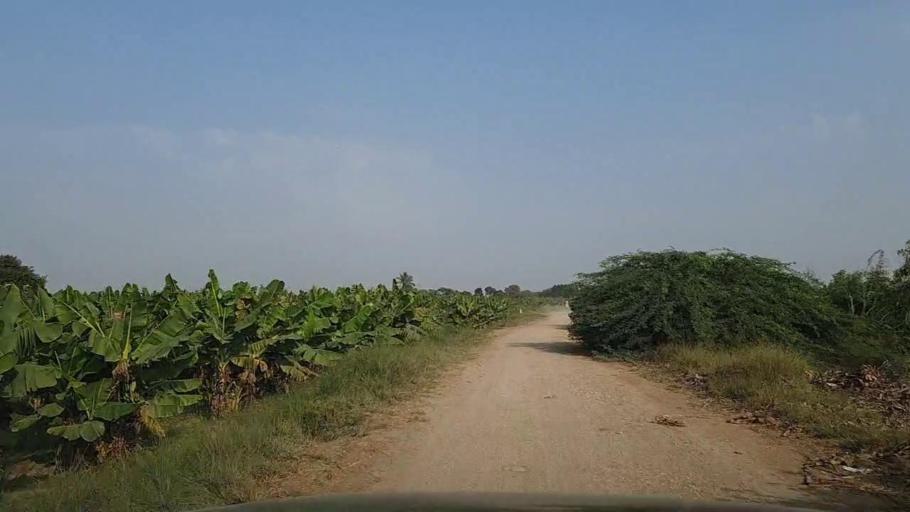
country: PK
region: Sindh
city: Thatta
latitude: 24.6438
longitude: 67.9436
